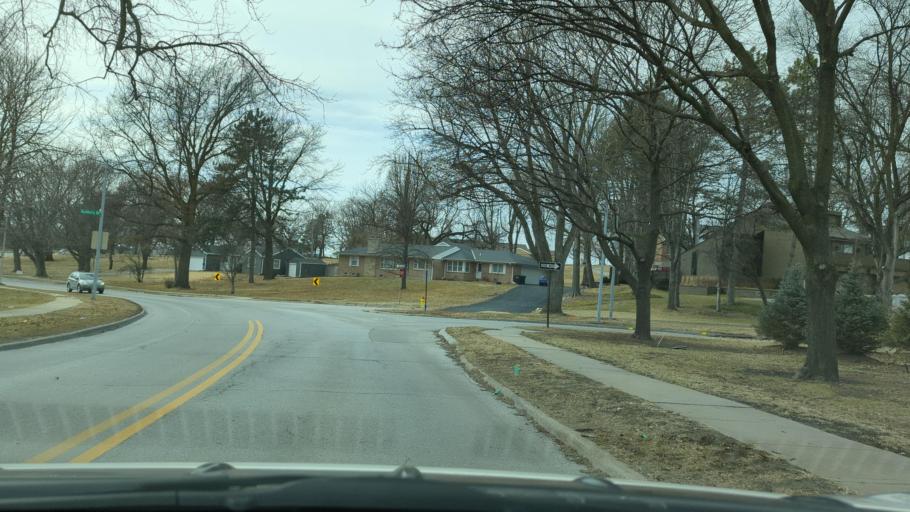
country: US
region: Nebraska
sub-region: Douglas County
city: Ralston
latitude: 41.2642
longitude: -96.0171
